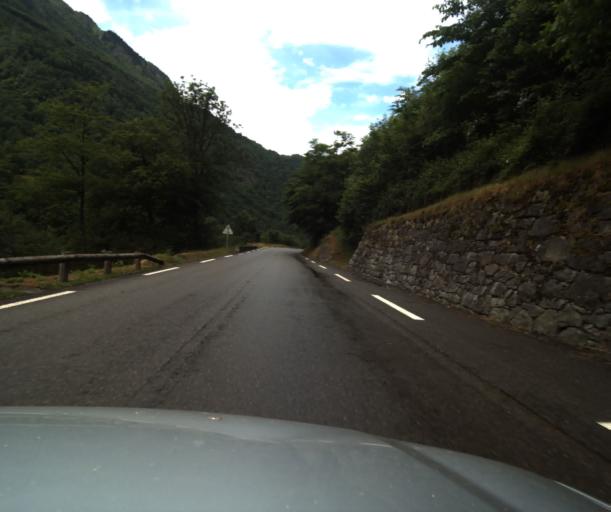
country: FR
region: Midi-Pyrenees
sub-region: Departement des Hautes-Pyrenees
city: Luz-Saint-Sauveur
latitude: 42.8395
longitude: -0.0049
